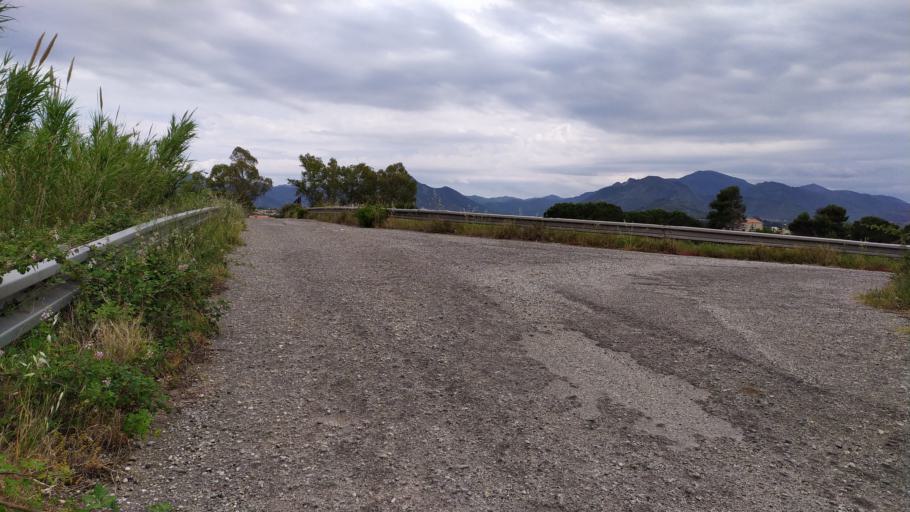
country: IT
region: Sicily
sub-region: Messina
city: San Filippo del Mela
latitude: 38.1861
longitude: 15.2598
